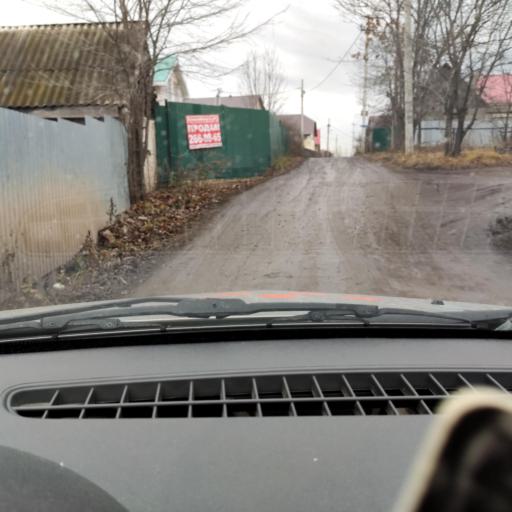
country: RU
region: Bashkortostan
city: Mikhaylovka
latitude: 54.8395
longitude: 55.9462
